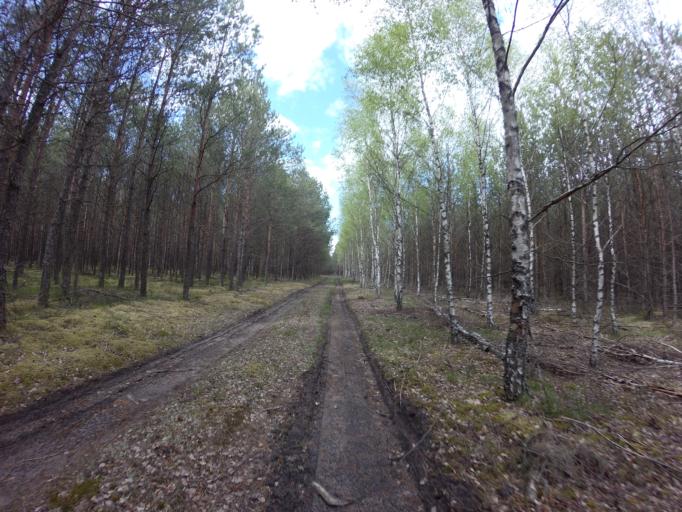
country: PL
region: West Pomeranian Voivodeship
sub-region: Powiat drawski
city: Kalisz Pomorski
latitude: 53.1794
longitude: 15.9767
